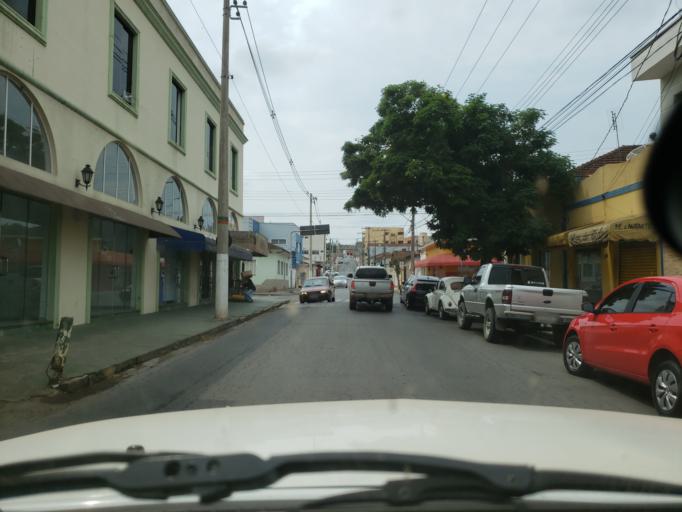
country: BR
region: Minas Gerais
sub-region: Jacutinga
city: Jacutinga
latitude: -22.2834
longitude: -46.6104
